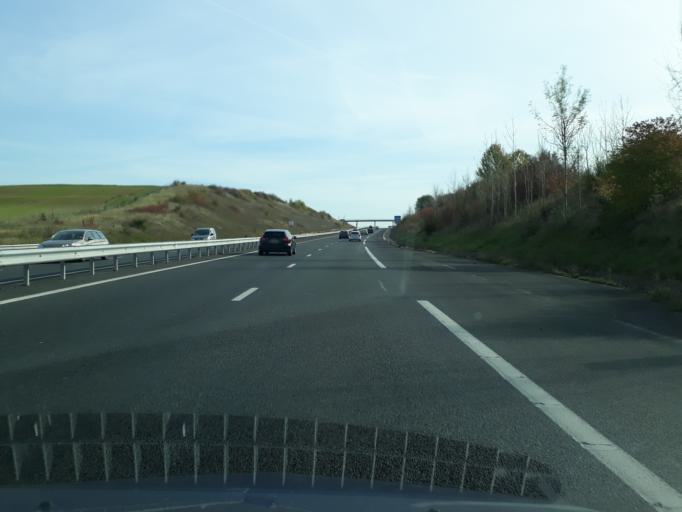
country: FR
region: Bourgogne
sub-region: Departement de l'Yonne
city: Thorigny-sur-Oreuse
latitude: 48.2478
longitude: 3.5373
